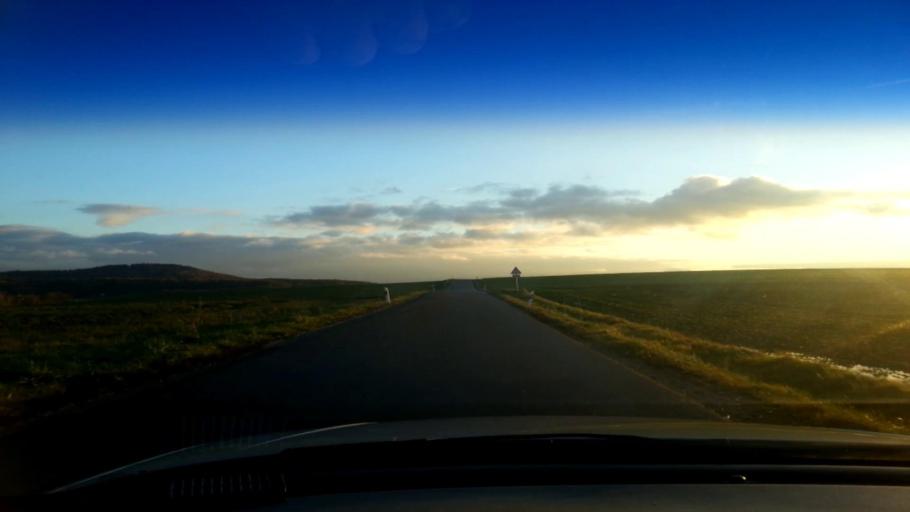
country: DE
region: Bavaria
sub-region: Upper Franconia
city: Buttenheim
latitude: 49.8185
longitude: 11.0543
